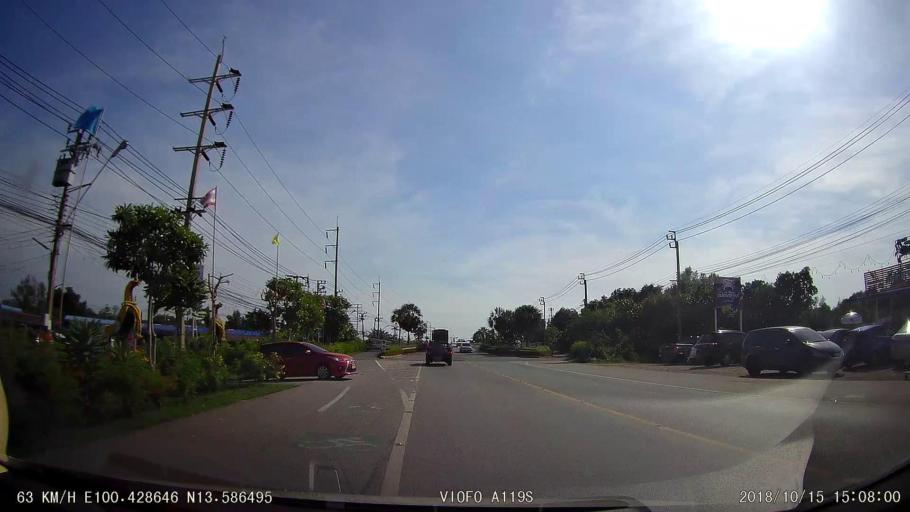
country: TH
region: Bangkok
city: Bang Khun Thian
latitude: 13.5864
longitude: 100.4286
